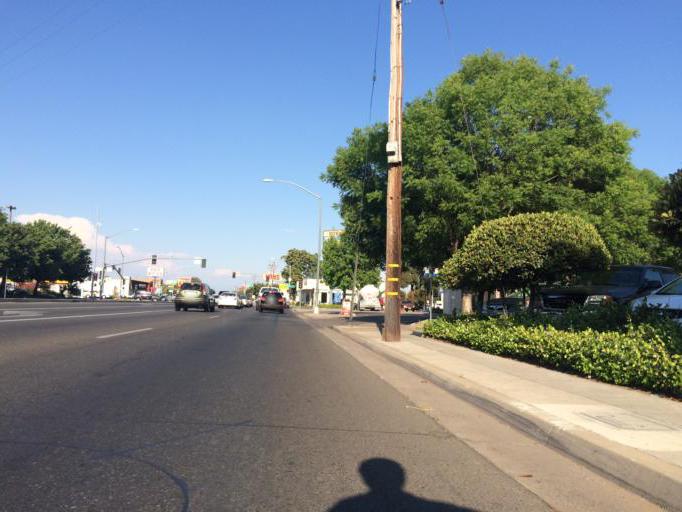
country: US
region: California
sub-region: Fresno County
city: Sunnyside
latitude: 36.7357
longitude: -119.7014
